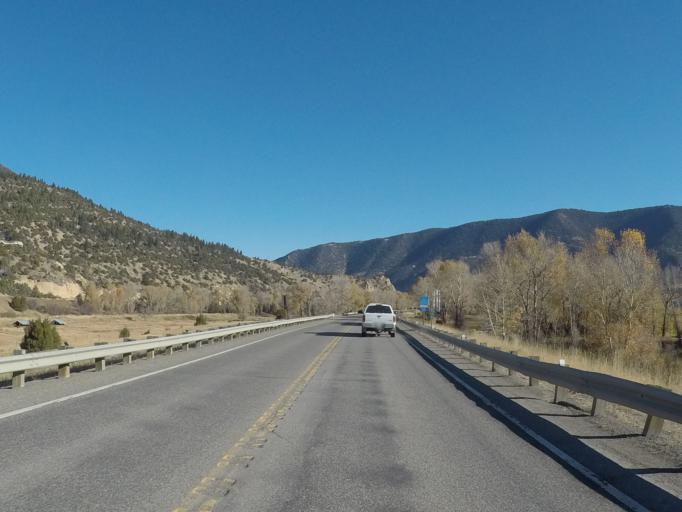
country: US
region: Montana
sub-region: Park County
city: Livingston
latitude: 45.5749
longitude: -110.5864
